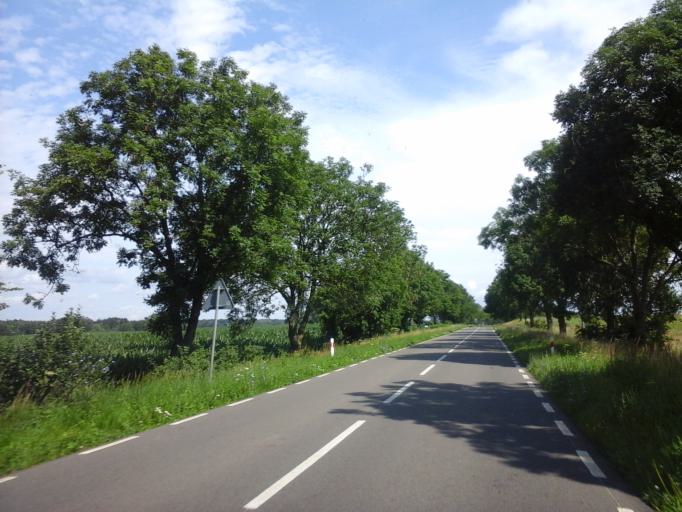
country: PL
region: West Pomeranian Voivodeship
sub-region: Powiat choszczenski
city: Recz
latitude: 53.2990
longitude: 15.5570
